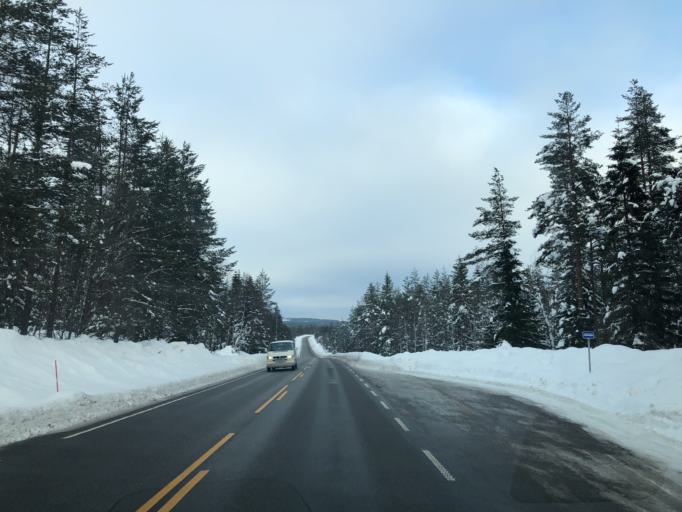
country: NO
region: Hedmark
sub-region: Trysil
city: Innbygda
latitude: 61.1893
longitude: 12.1989
